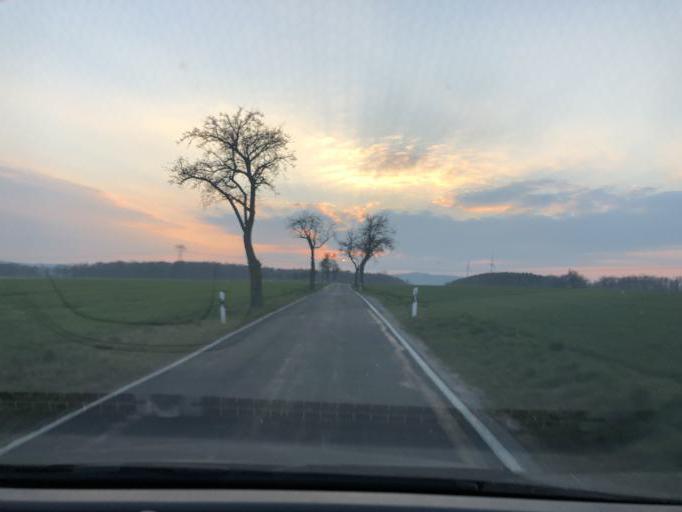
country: DE
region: Saxony
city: Panschwitz-Kuckau
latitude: 51.2306
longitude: 14.1781
